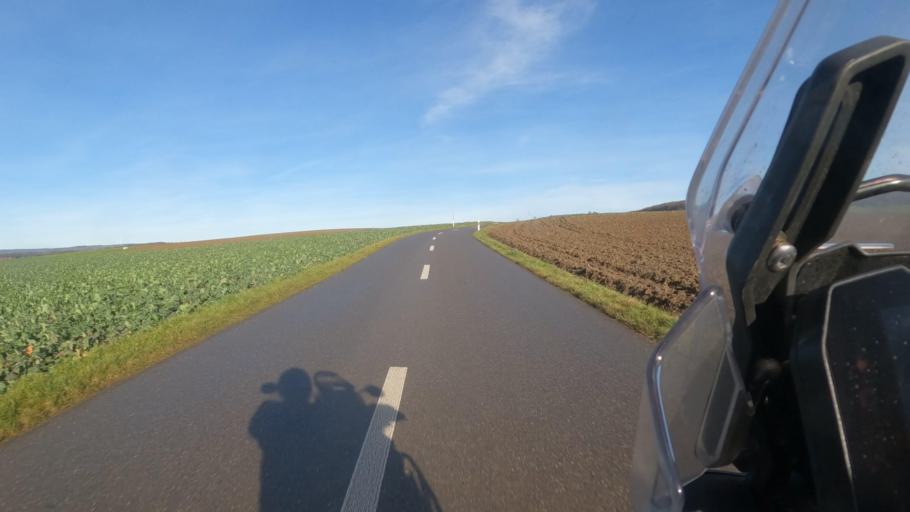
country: DE
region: Baden-Wuerttemberg
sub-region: Freiburg Region
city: Busingen
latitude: 47.6968
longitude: 8.7178
